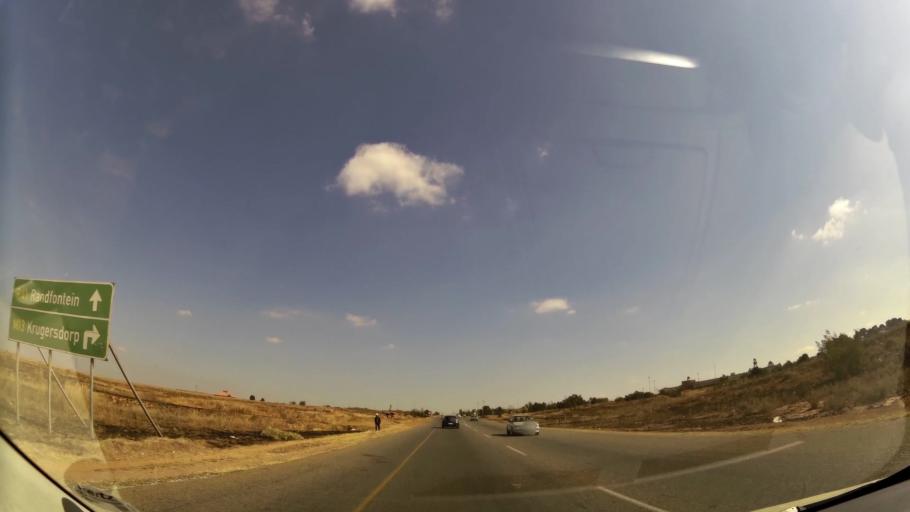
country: ZA
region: Gauteng
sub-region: West Rand District Municipality
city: Randfontein
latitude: -26.1788
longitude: 27.7624
